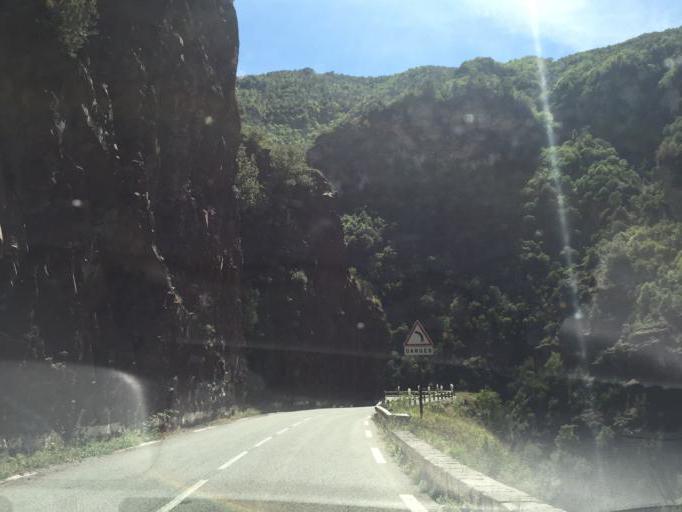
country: FR
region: Provence-Alpes-Cote d'Azur
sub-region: Departement des Alpes-Maritimes
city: Saint-Martin-Vesubie
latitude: 44.0555
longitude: 7.1193
